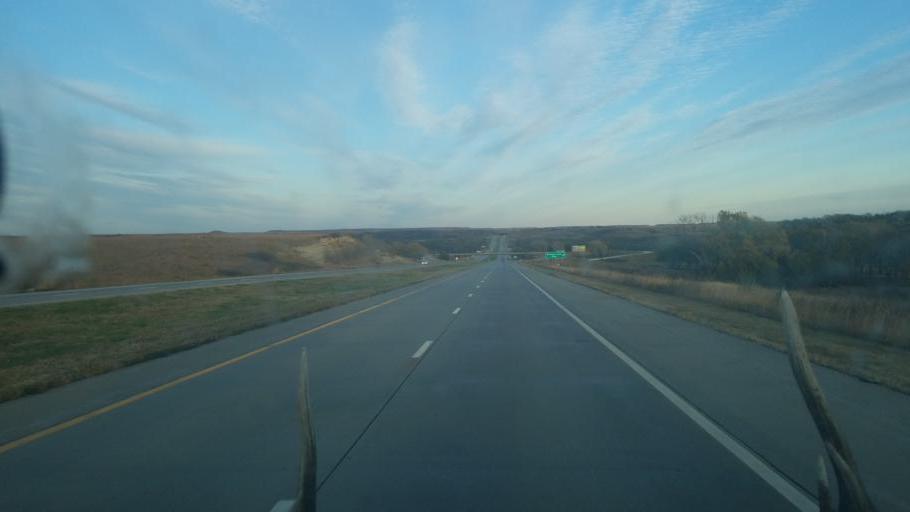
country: US
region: Kansas
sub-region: Riley County
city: Ogden
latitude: 39.0662
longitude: -96.6652
